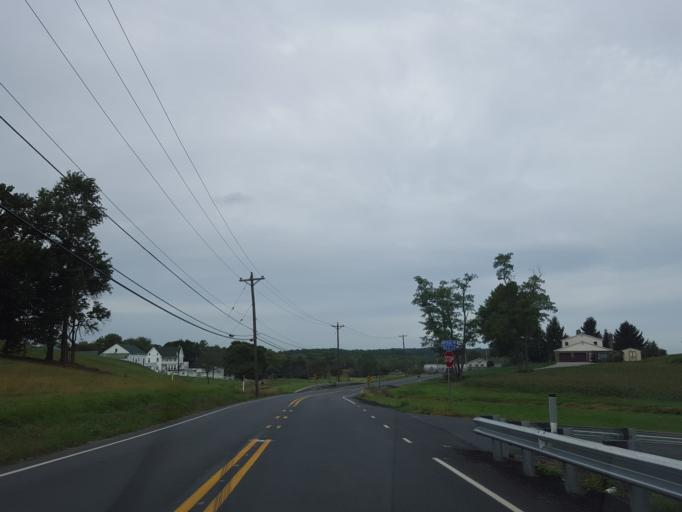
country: US
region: Pennsylvania
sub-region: York County
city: Grantley
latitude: 39.9164
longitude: -76.7388
